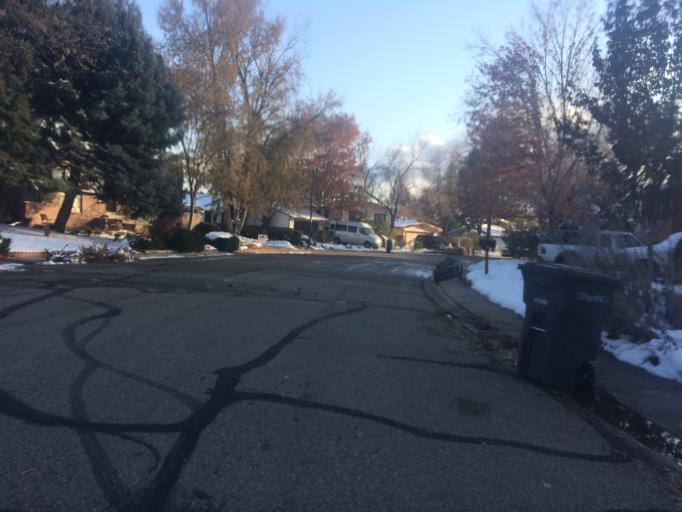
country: US
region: Colorado
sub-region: Boulder County
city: Lafayette
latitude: 39.9896
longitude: -105.1054
